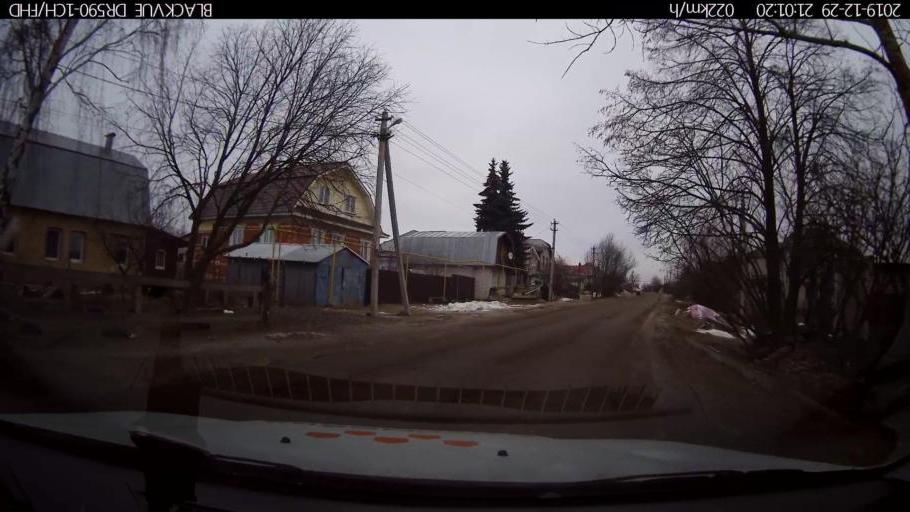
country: RU
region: Nizjnij Novgorod
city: Afonino
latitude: 56.1877
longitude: 43.9896
